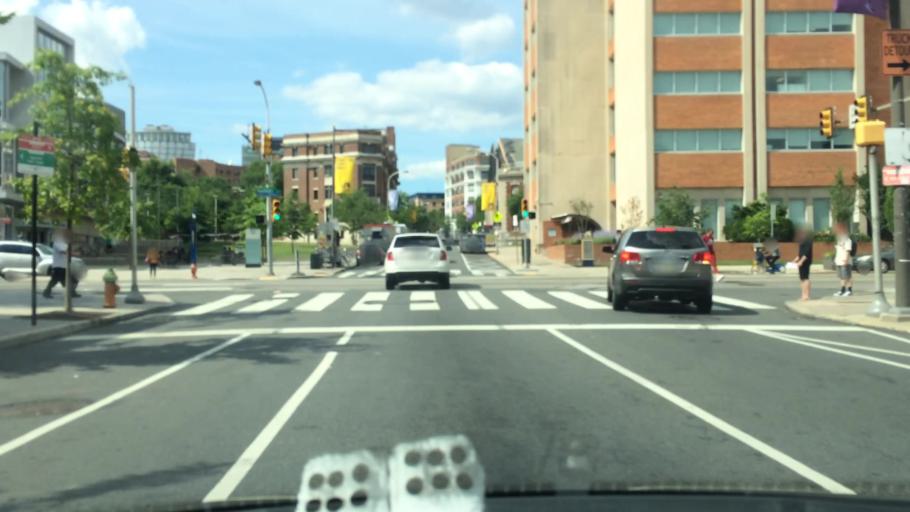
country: US
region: Pennsylvania
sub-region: Philadelphia County
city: Philadelphia
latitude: 39.9553
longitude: -75.1895
